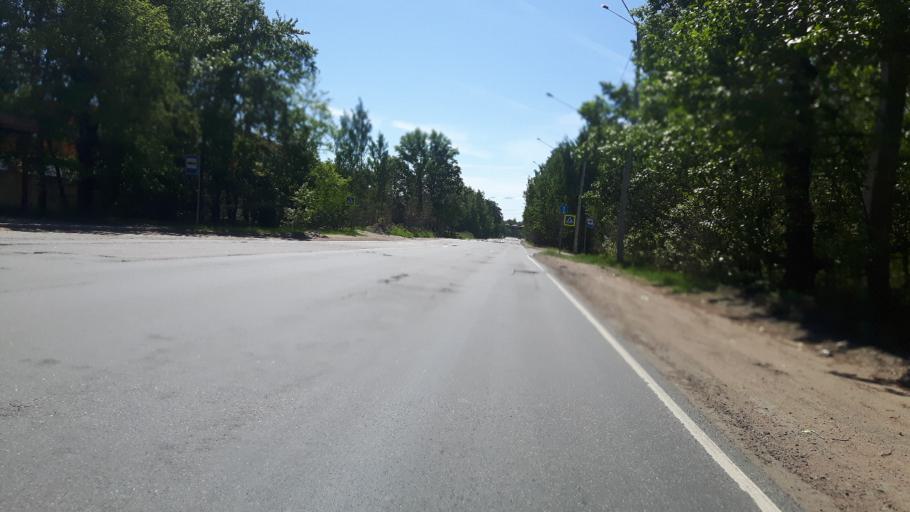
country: RU
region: Leningrad
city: Sosnovyy Bor
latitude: 59.8684
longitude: 29.0767
